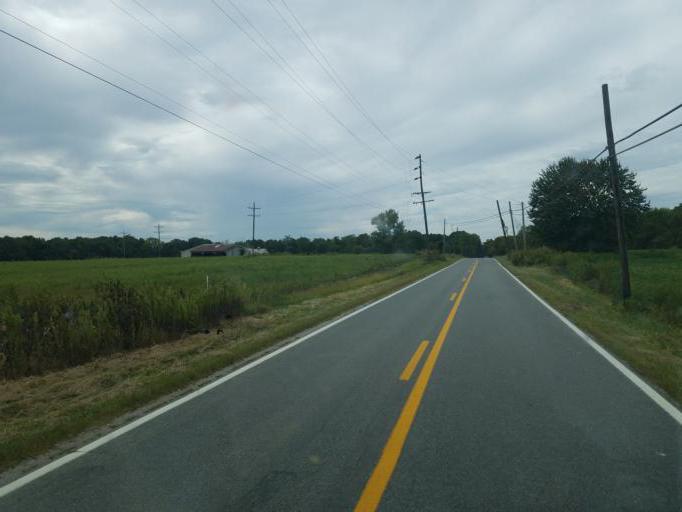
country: US
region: Ohio
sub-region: Delaware County
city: Sunbury
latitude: 40.2462
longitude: -82.8400
